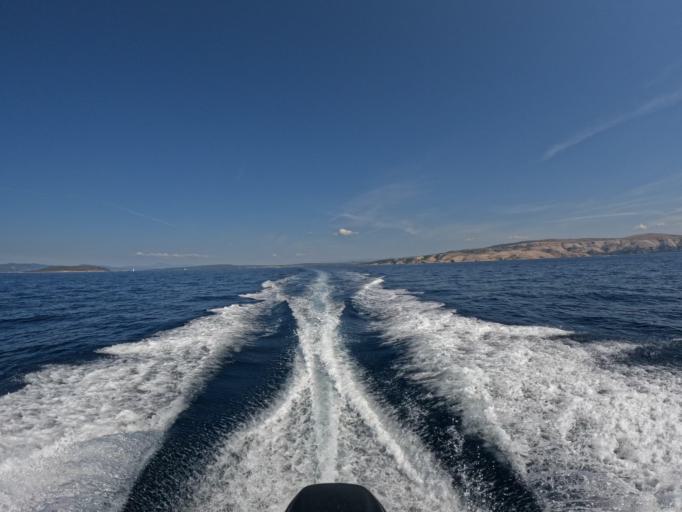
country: HR
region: Primorsko-Goranska
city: Punat
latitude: 44.9237
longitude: 14.6204
